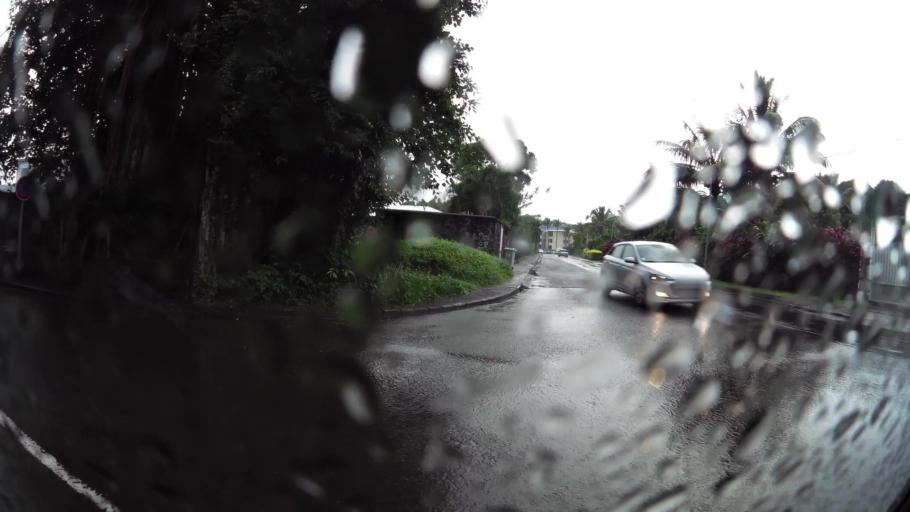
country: RE
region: Reunion
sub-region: Reunion
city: Saint-Benoit
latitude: -21.0355
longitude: 55.7085
